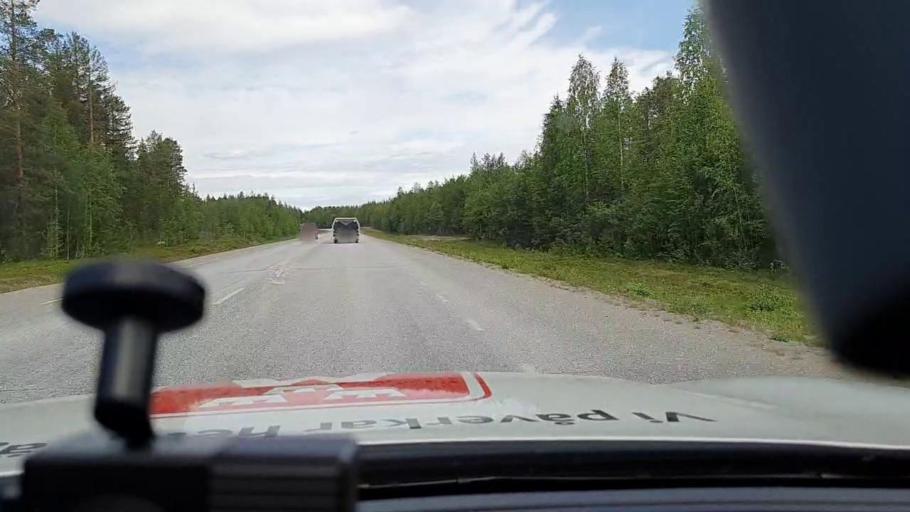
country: SE
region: Norrbotten
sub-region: Jokkmokks Kommun
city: Jokkmokk
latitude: 66.5059
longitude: 20.2494
